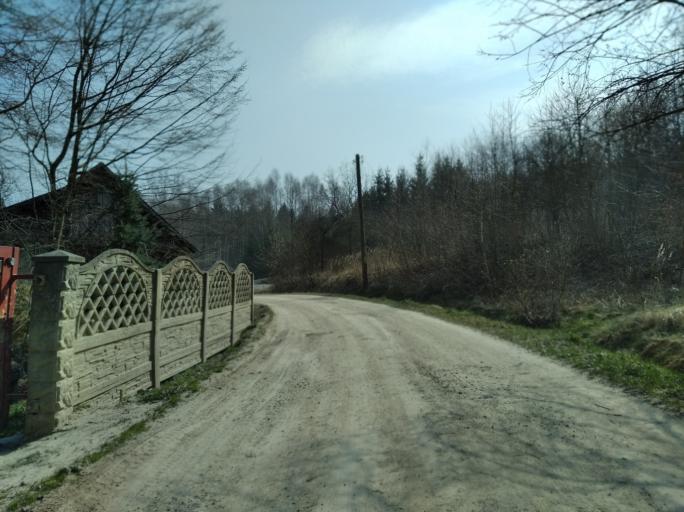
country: PL
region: Subcarpathian Voivodeship
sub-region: Powiat strzyzowski
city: Wysoka Strzyzowska
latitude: 49.8327
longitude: 21.7779
